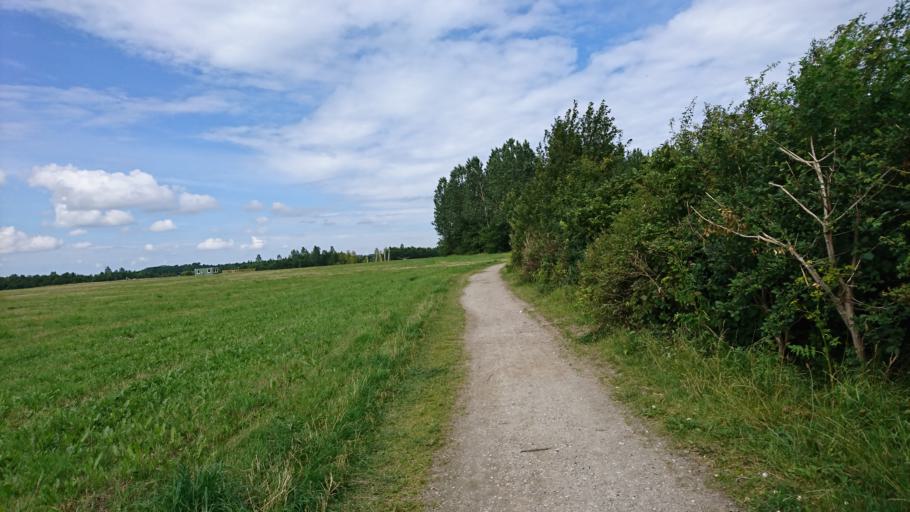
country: DK
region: Capital Region
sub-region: Ballerup Kommune
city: Ballerup
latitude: 55.7161
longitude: 12.3855
